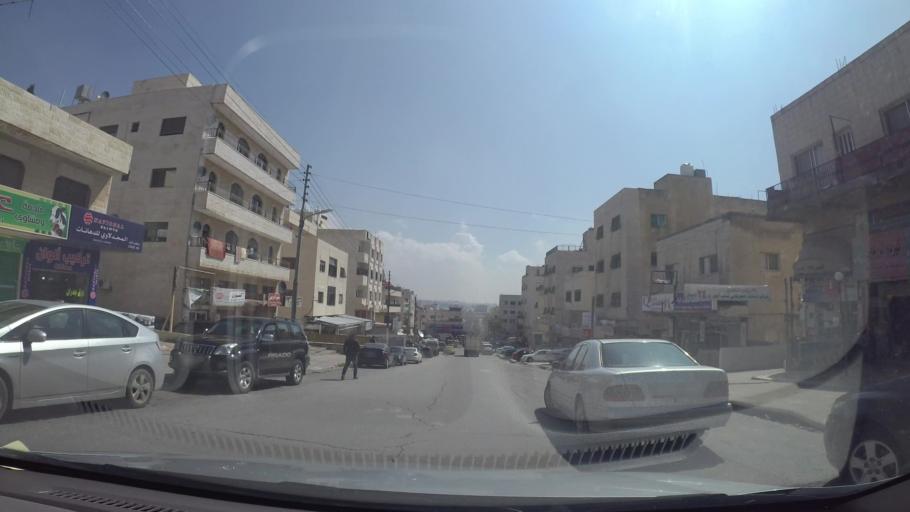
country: JO
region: Amman
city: Al Bunayyat ash Shamaliyah
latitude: 31.9257
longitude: 35.9024
